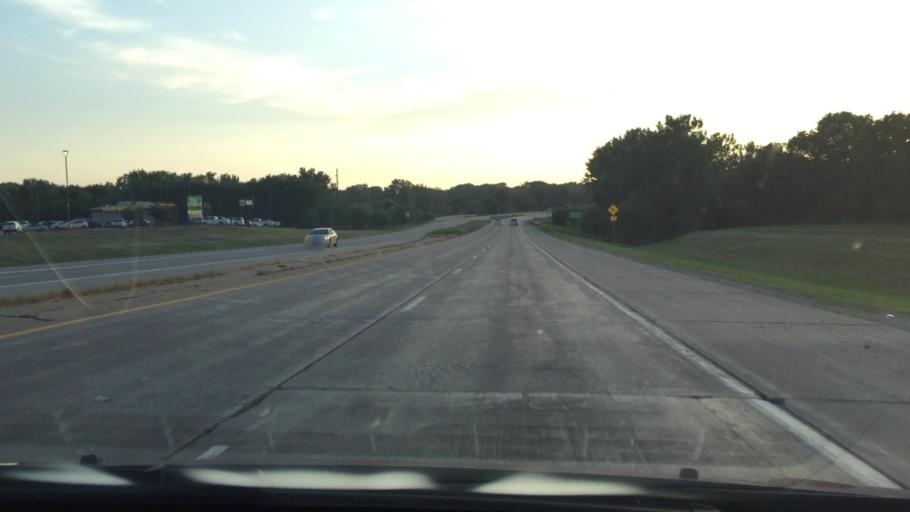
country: US
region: Iowa
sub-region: Muscatine County
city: Muscatine
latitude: 41.4527
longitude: -91.0355
